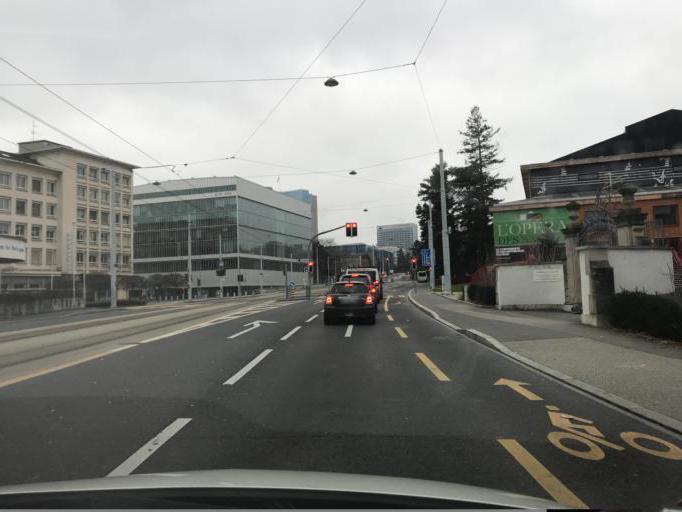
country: CH
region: Geneva
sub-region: Geneva
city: Le Grand-Saconnex
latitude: 46.2212
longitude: 6.1411
